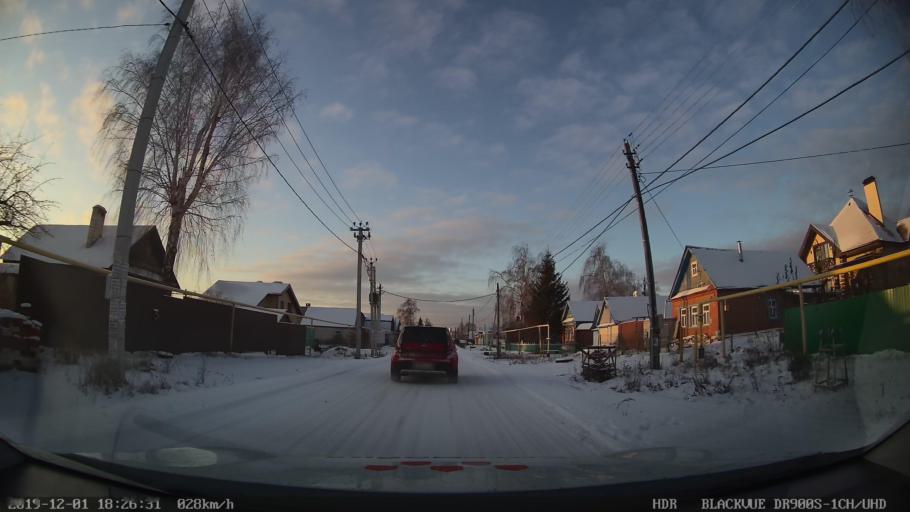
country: RU
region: Tatarstan
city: Vysokaya Gora
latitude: 55.8072
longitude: 49.2568
